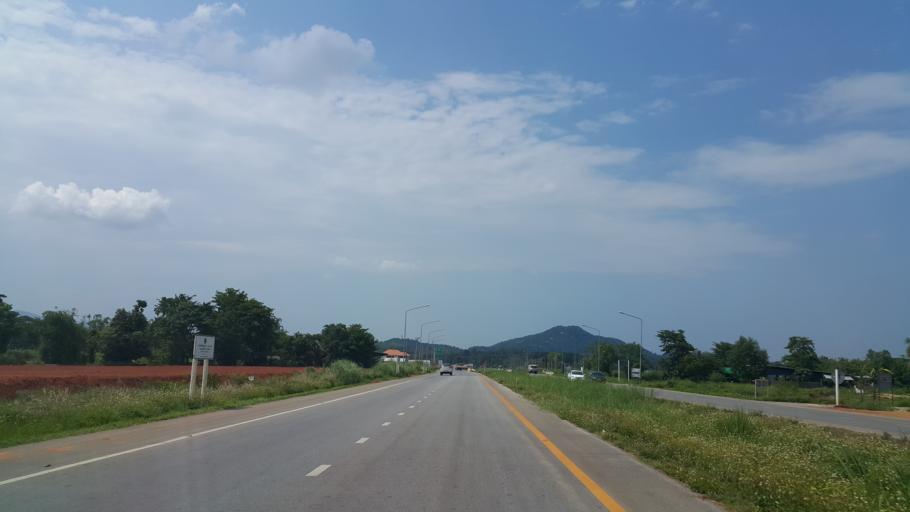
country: TH
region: Chiang Rai
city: Chiang Rai
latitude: 20.0003
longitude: 99.8928
